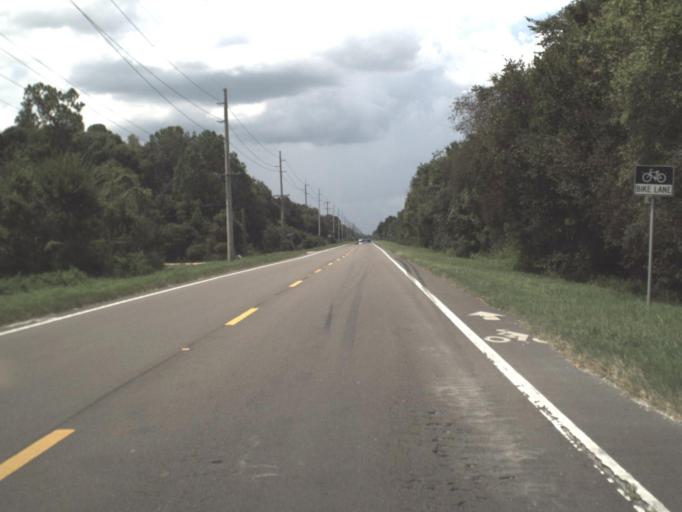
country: US
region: Florida
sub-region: Pasco County
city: Crystal Springs
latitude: 28.1411
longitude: -82.1502
